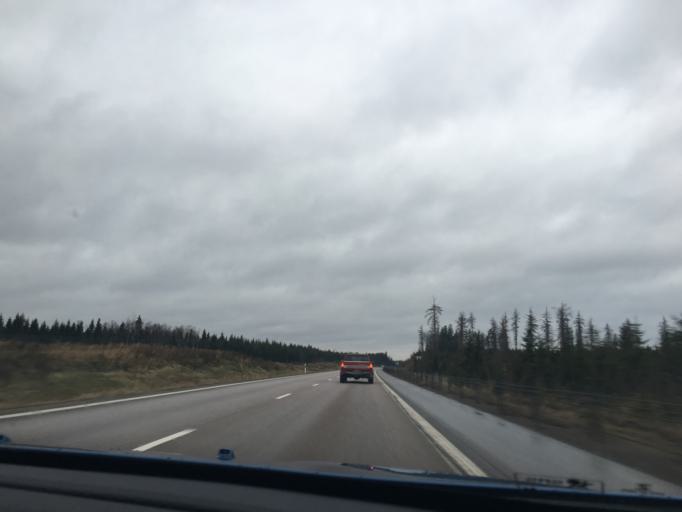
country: SE
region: Uppsala
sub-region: Tierps Kommun
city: Tierp
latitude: 60.4208
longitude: 17.4431
